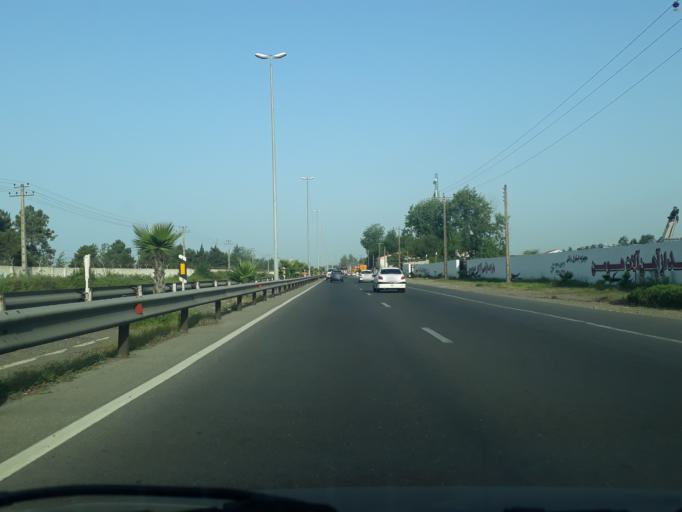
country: IR
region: Gilan
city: Bandar-e Anzali
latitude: 37.4583
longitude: 49.6032
